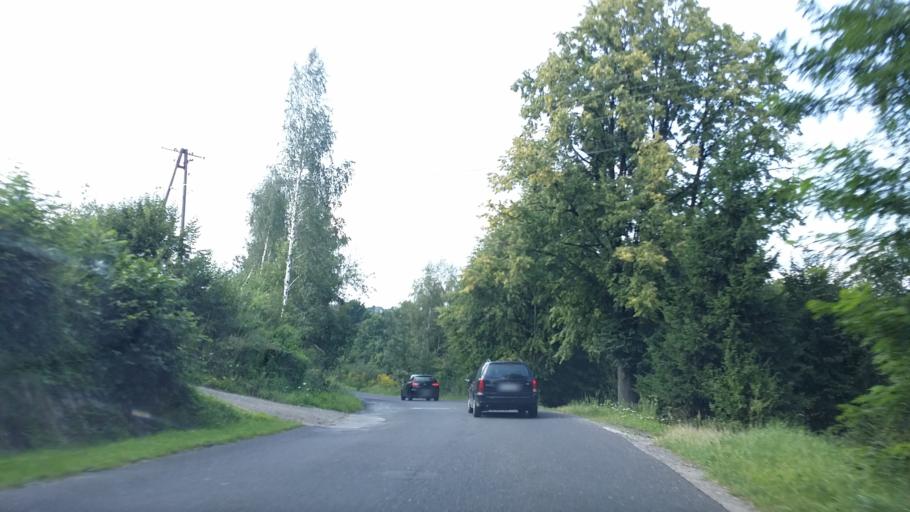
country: PL
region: Lesser Poland Voivodeship
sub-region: Powiat myslenicki
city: Brzaczowice
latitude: 49.9069
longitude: 20.0348
